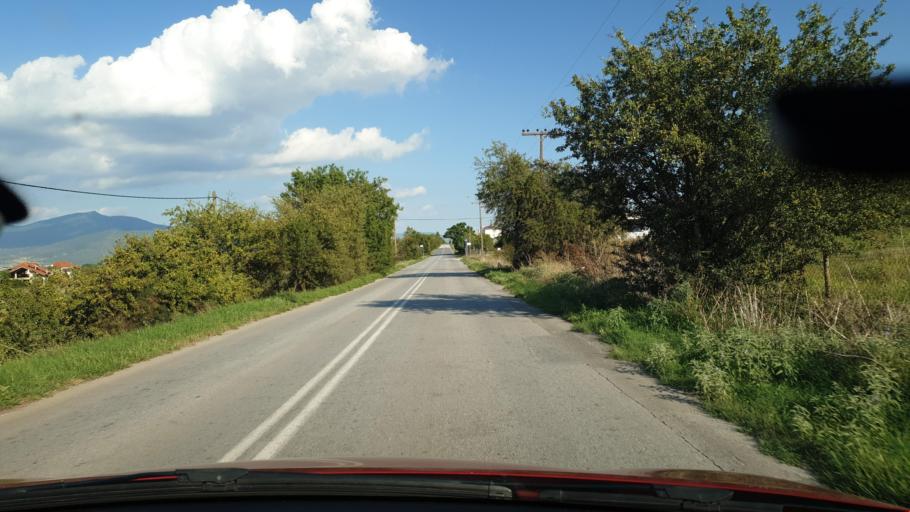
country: GR
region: Central Macedonia
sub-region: Nomos Thessalonikis
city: Agia Paraskevi
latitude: 40.4815
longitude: 23.0634
